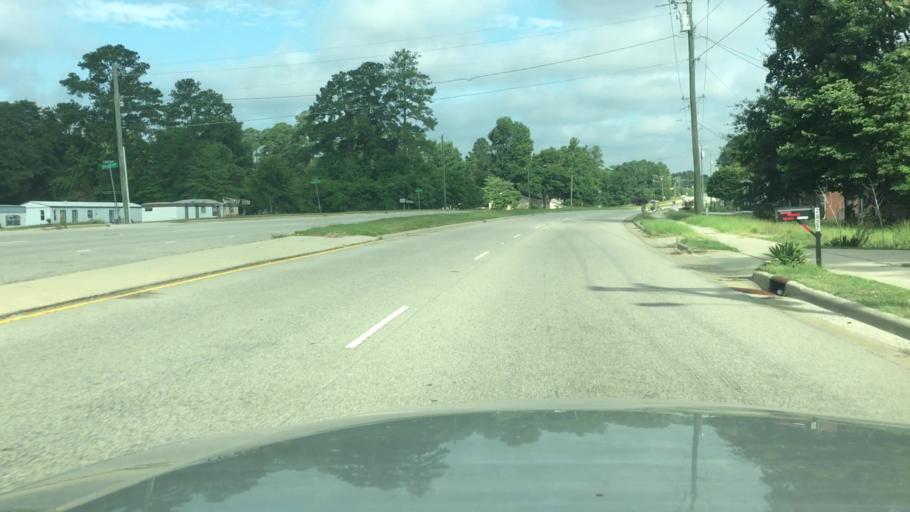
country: US
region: North Carolina
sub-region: Cumberland County
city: Hope Mills
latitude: 34.9919
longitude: -78.9618
